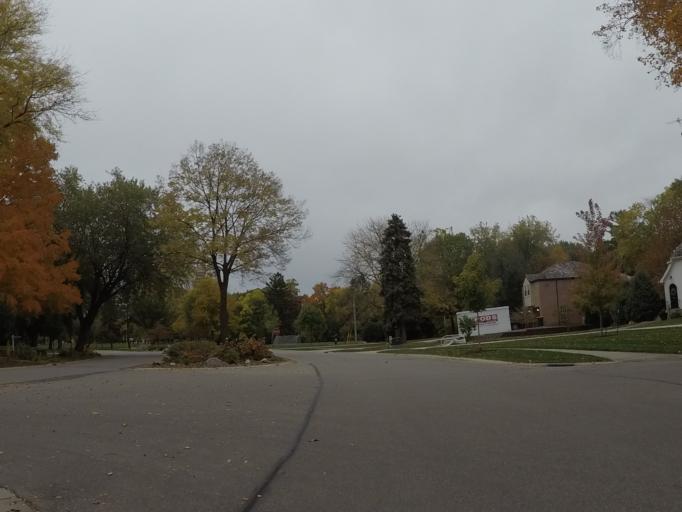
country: US
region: Wisconsin
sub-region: Dane County
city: Maple Bluff
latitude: 43.1056
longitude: -89.3668
